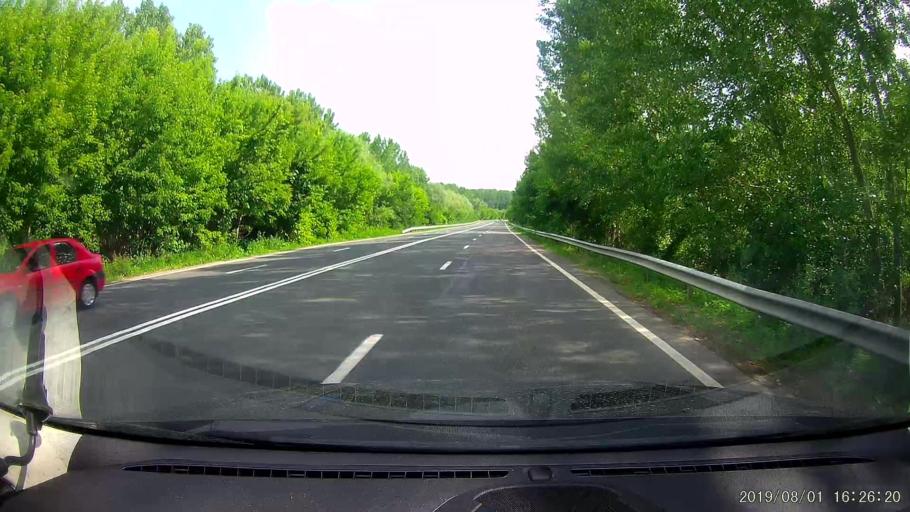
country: RO
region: Calarasi
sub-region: Municipiul Calarasi
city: Calarasi
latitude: 44.1822
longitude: 27.3218
